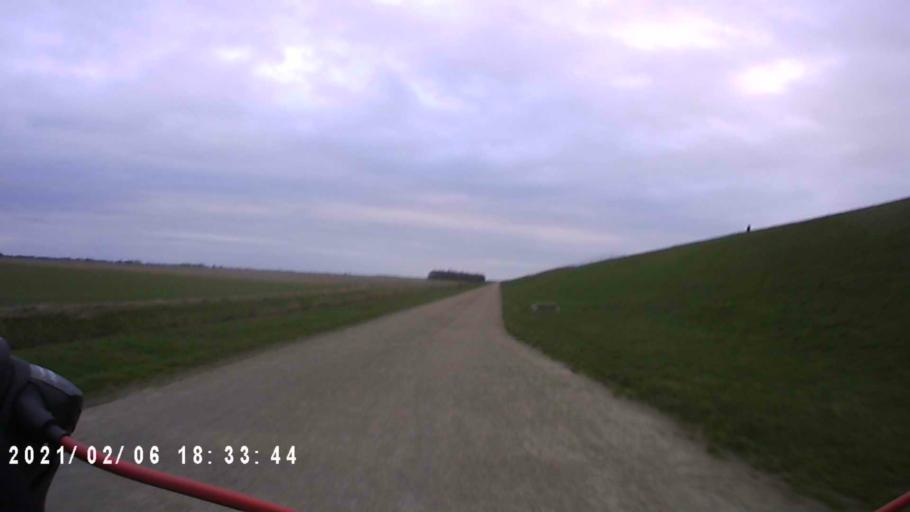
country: DE
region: Lower Saxony
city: Borkum
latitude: 53.4510
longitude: 6.6470
